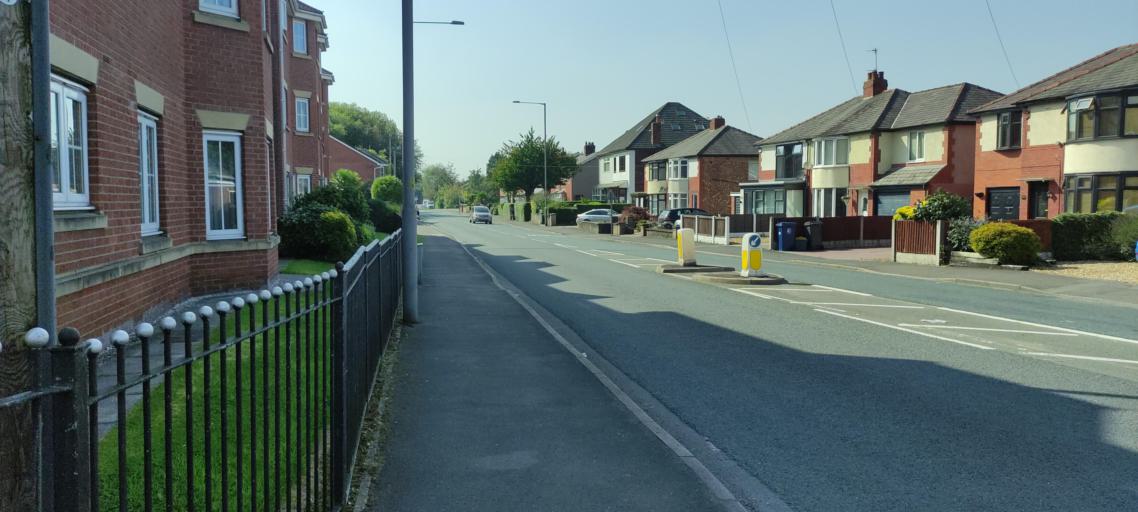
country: GB
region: England
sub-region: Lancashire
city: Clayton-le-Woods
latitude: 53.7293
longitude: -2.6692
